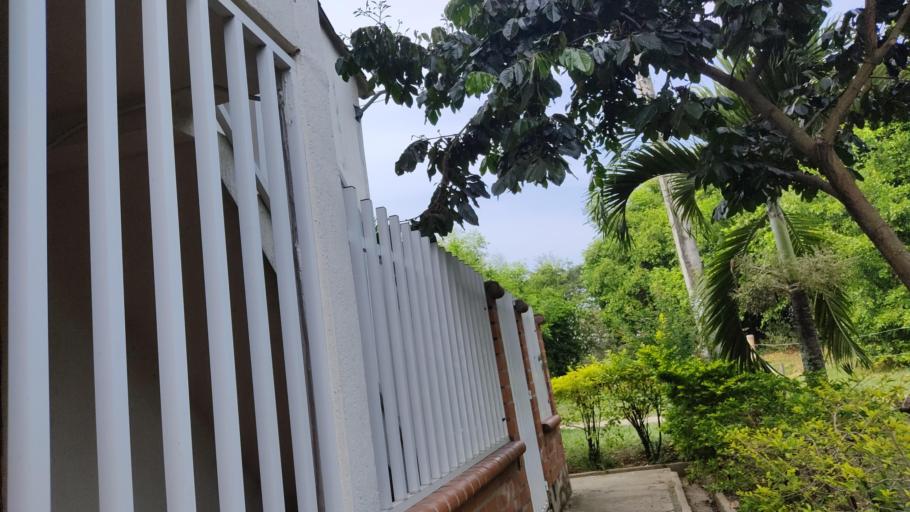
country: CO
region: Valle del Cauca
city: Jamundi
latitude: 3.2382
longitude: -76.5105
